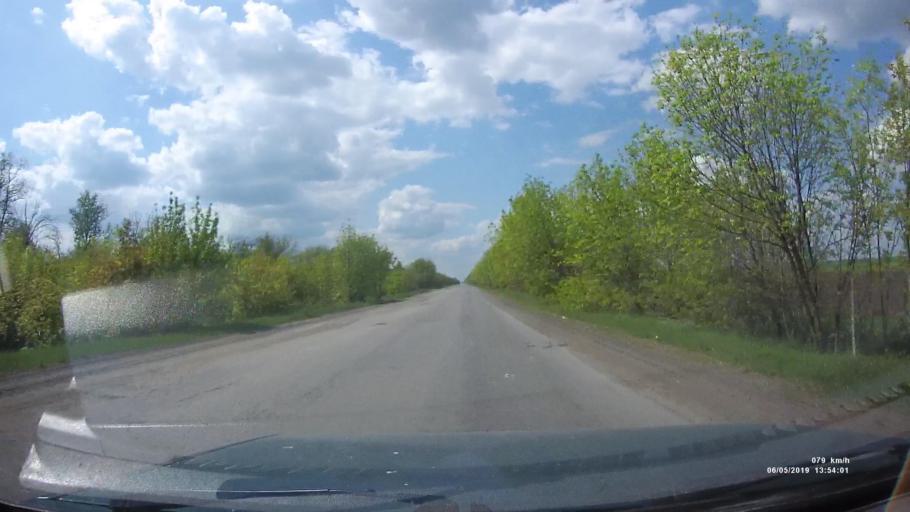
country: RU
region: Rostov
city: Melikhovskaya
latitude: 47.6720
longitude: 40.4534
